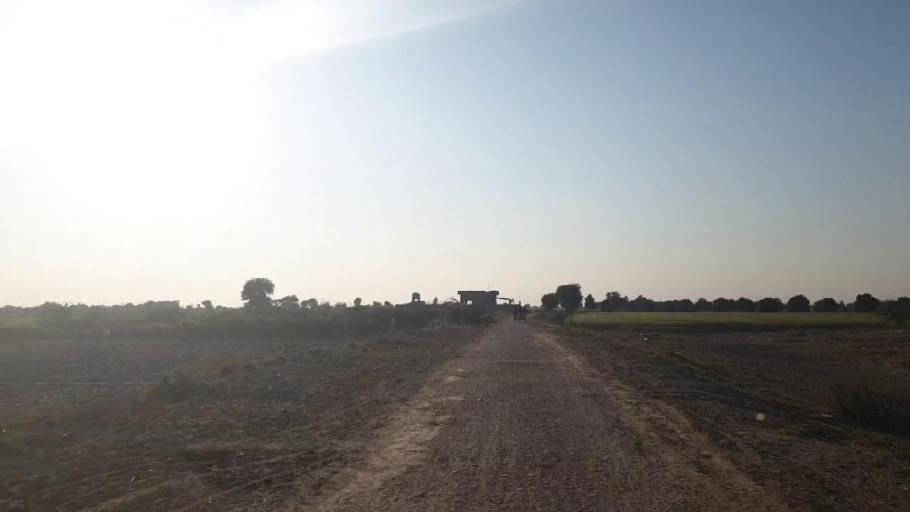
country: PK
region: Sindh
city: Shahpur Chakar
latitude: 26.0606
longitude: 68.6637
